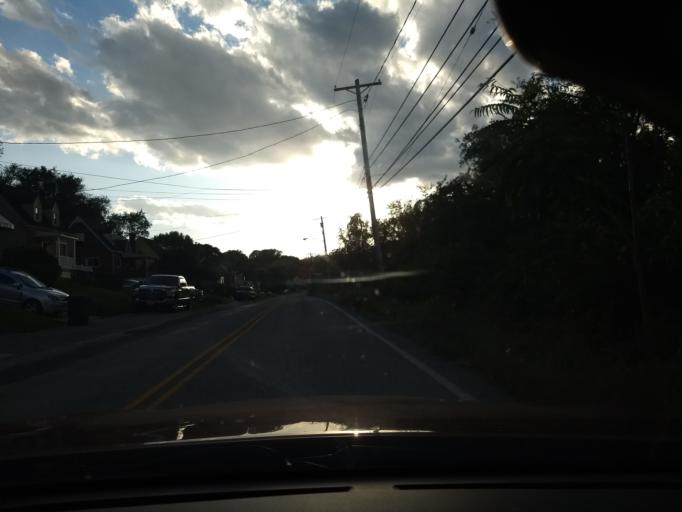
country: US
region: Pennsylvania
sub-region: Allegheny County
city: Dravosburg
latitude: 40.3588
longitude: -79.8891
